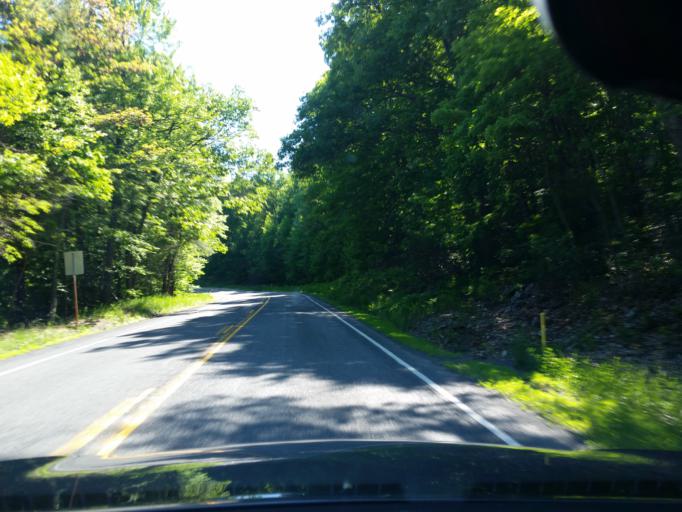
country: US
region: Pennsylvania
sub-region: Lycoming County
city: Duboistown
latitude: 41.1455
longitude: -77.0539
